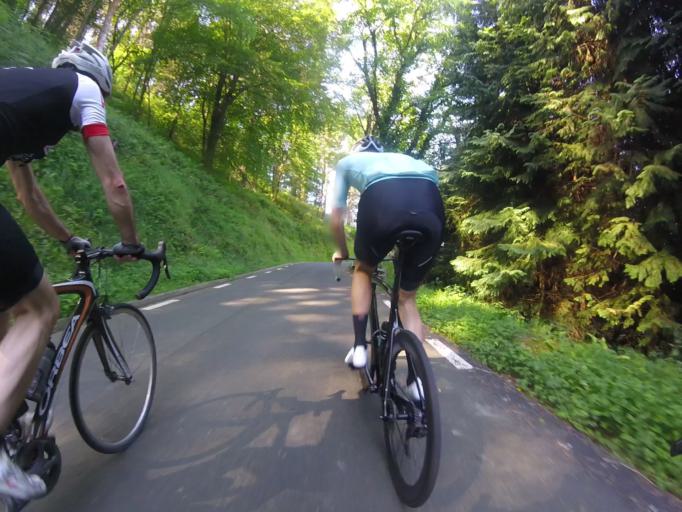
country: ES
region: Basque Country
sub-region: Provincia de Guipuzcoa
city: Beizama
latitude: 43.1369
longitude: -2.2236
